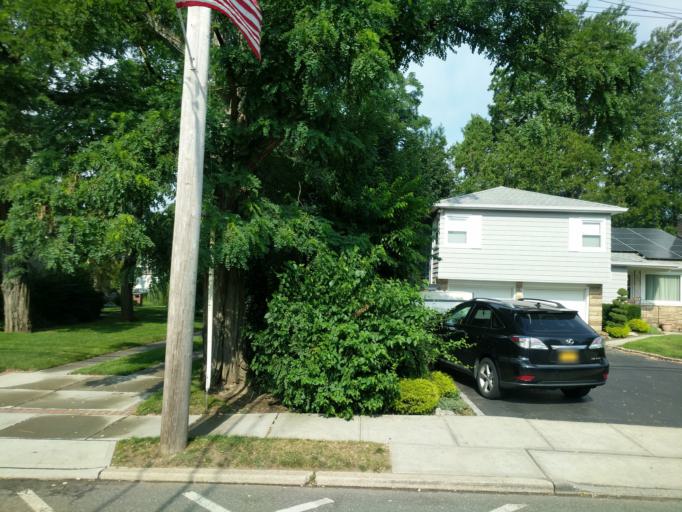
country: US
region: New York
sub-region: Nassau County
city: Malverne
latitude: 40.6733
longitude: -73.6702
